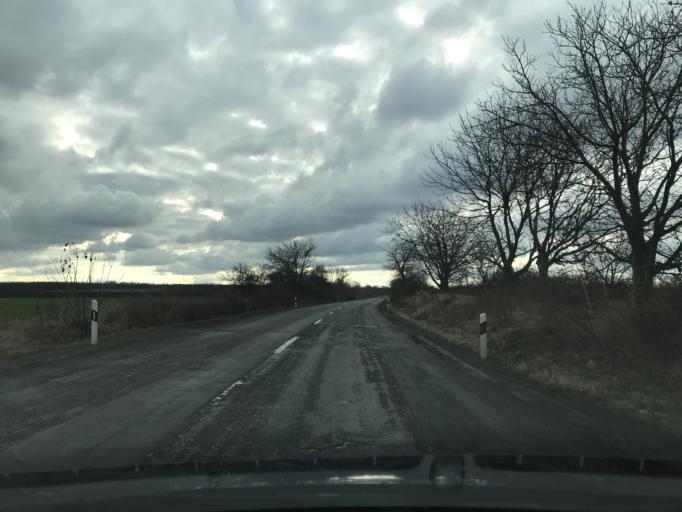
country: HU
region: Bacs-Kiskun
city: Csaszartoltes
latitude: 46.3913
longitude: 19.1631
